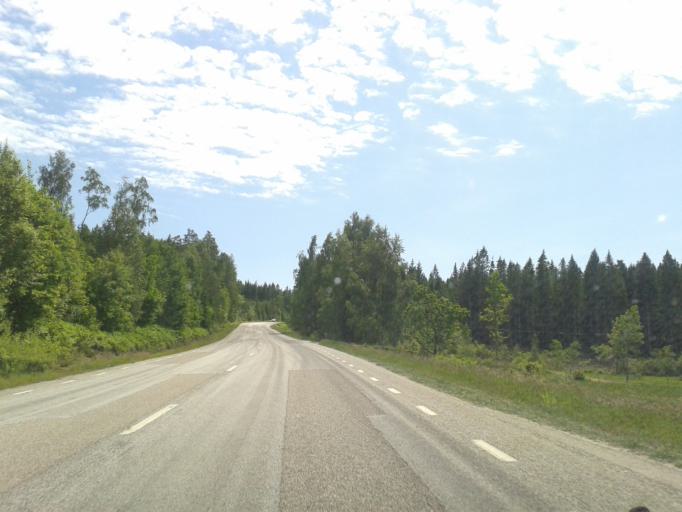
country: SE
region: Vaestra Goetaland
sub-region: Uddevalla Kommun
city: Ljungskile
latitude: 58.1758
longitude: 11.9621
